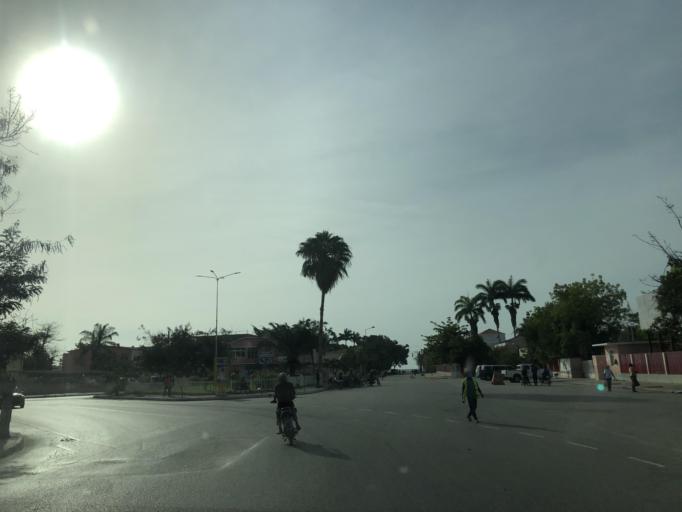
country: AO
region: Benguela
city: Benguela
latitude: -12.5732
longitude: 13.4025
